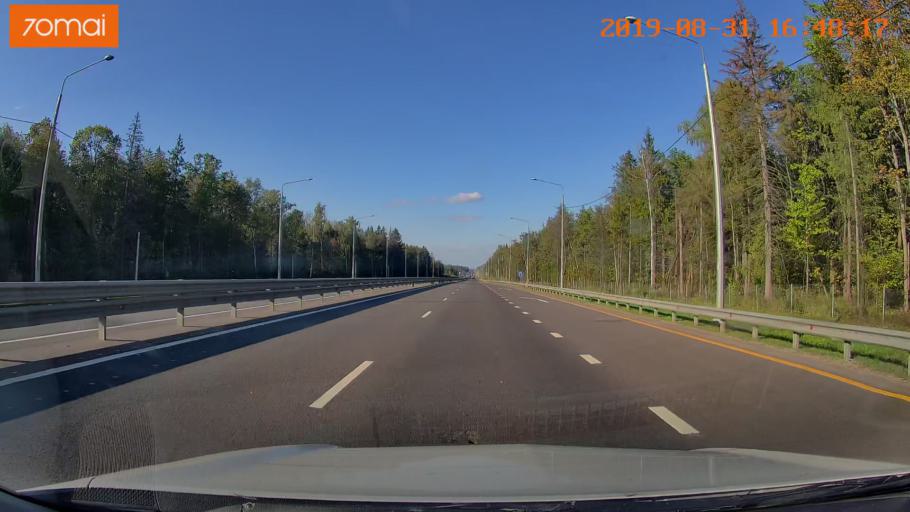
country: RU
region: Kaluga
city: Pyatovskiy
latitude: 54.6693
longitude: 36.1455
